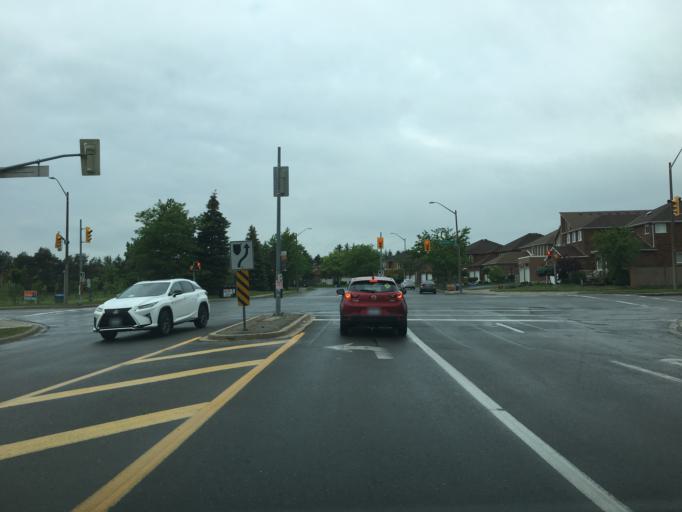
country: CA
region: Ontario
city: Markham
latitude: 43.8362
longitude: -79.2672
